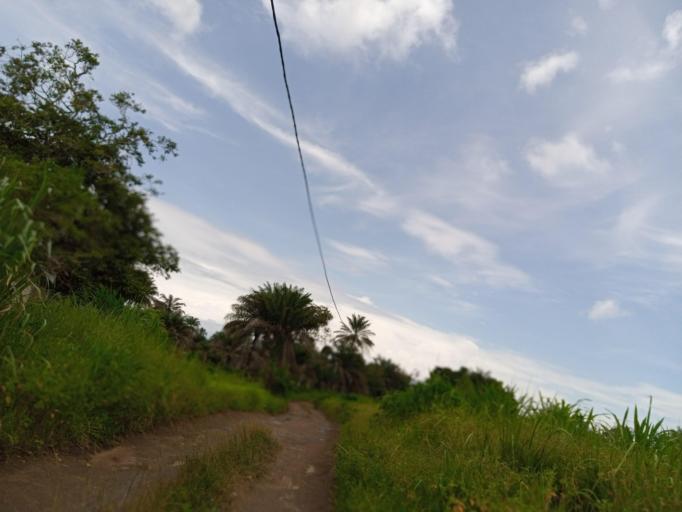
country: SL
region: Northern Province
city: Masoyila
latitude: 8.5923
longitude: -13.1682
